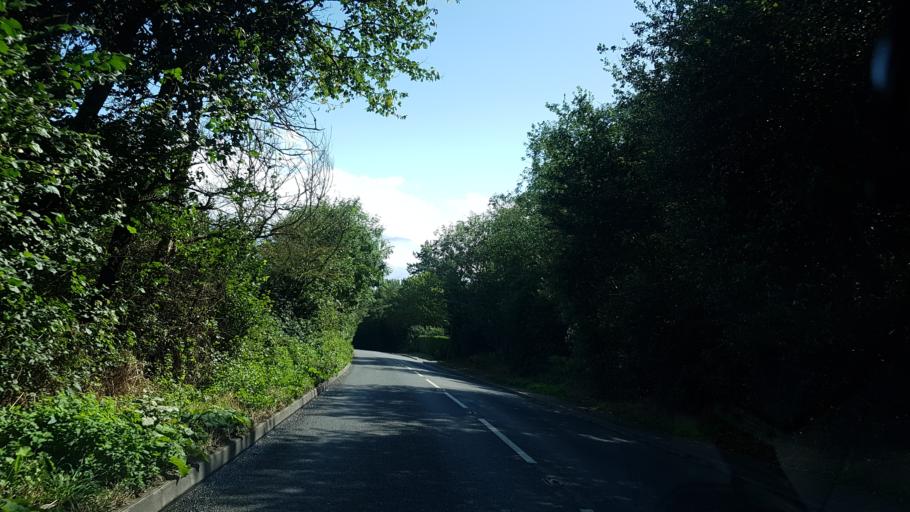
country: GB
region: England
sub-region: Surrey
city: West Byfleet
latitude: 51.3179
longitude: -0.5107
